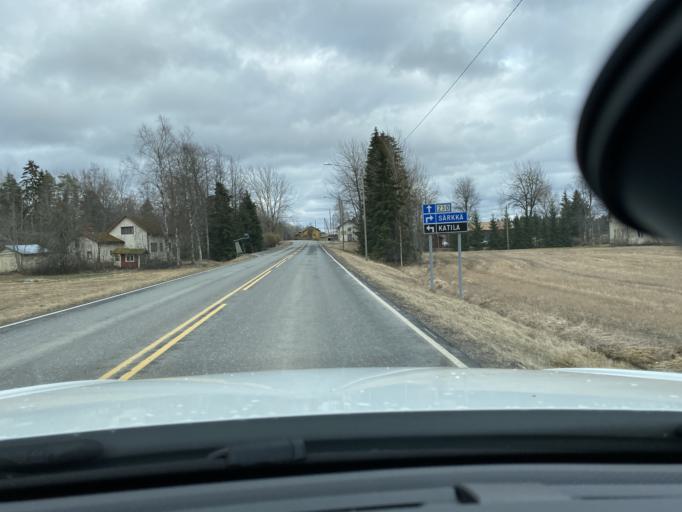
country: FI
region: Pirkanmaa
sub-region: Lounais-Pirkanmaa
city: Punkalaidun
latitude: 61.1014
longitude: 23.2015
